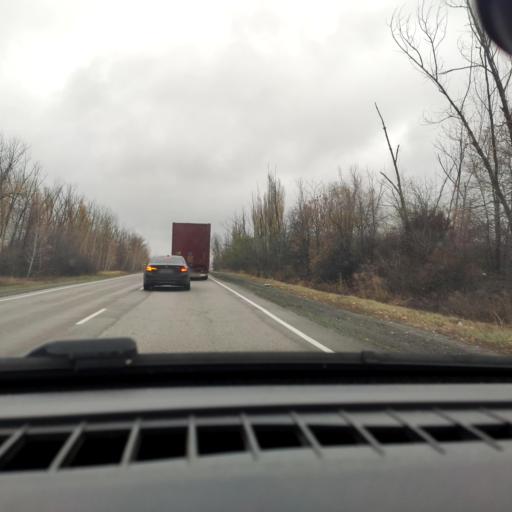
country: RU
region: Voronezj
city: Ostrogozhsk
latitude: 51.0167
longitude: 38.9855
